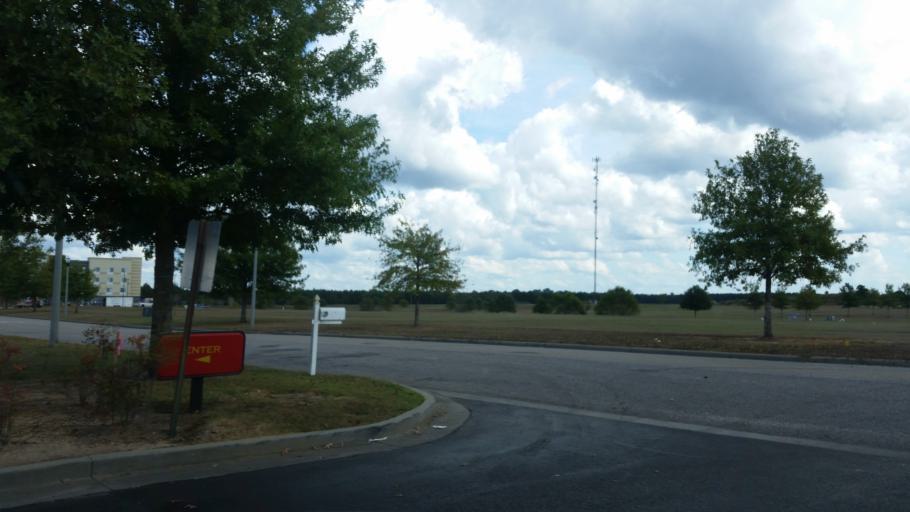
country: US
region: Alabama
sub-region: Escambia County
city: Atmore
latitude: 31.1060
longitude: -87.4757
